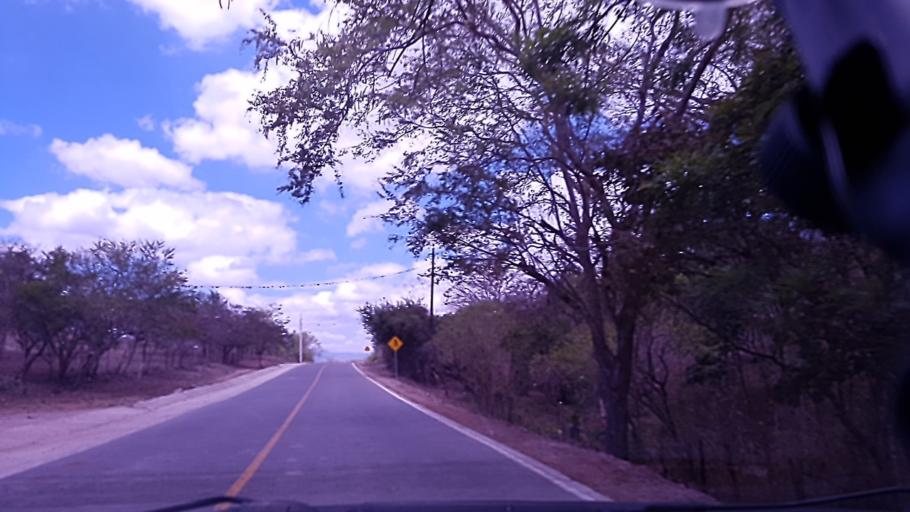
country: NI
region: Esteli
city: Condega
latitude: 13.3774
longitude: -86.3653
